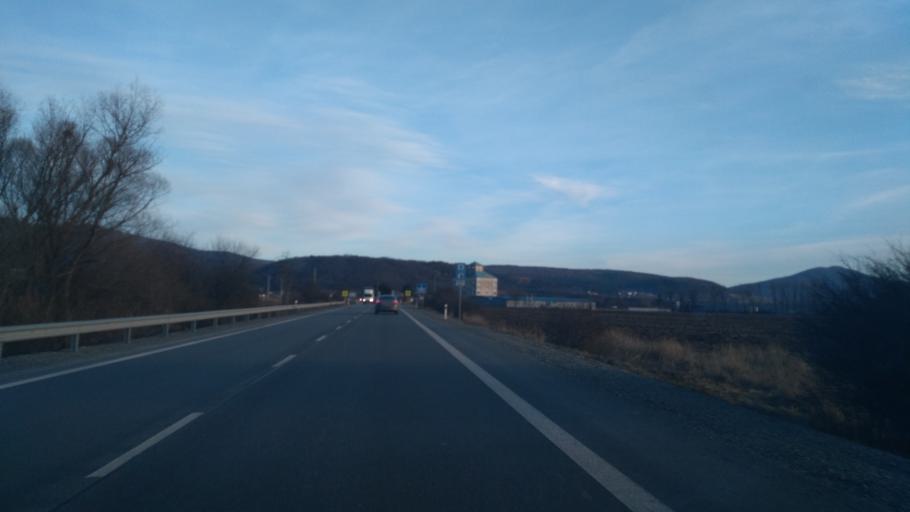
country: SK
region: Kosicky
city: Kosice
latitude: 48.7332
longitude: 21.4349
